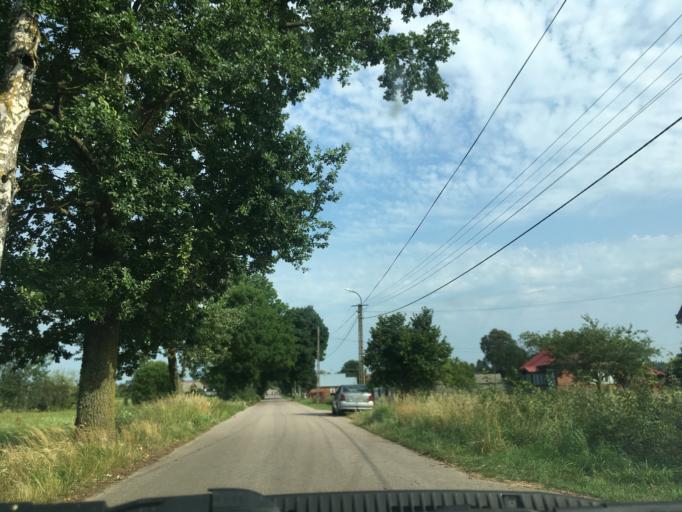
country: PL
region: Podlasie
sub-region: Powiat hajnowski
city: Bialowieza
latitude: 52.8982
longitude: 23.8326
